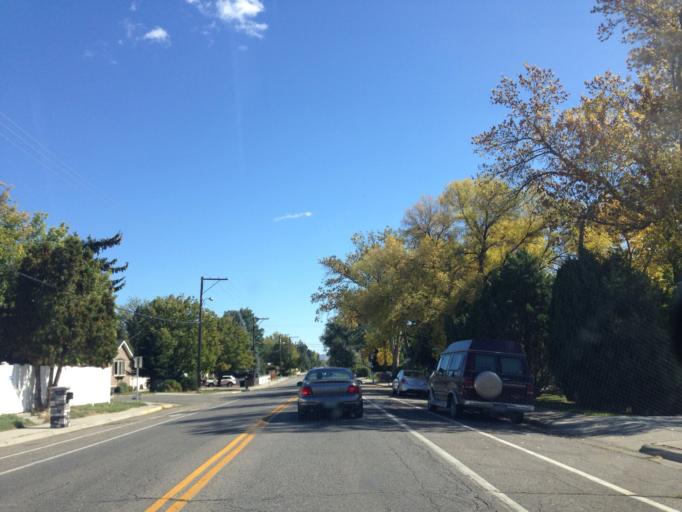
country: US
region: Montana
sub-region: Yellowstone County
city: Billings
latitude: 45.7950
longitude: -108.5749
